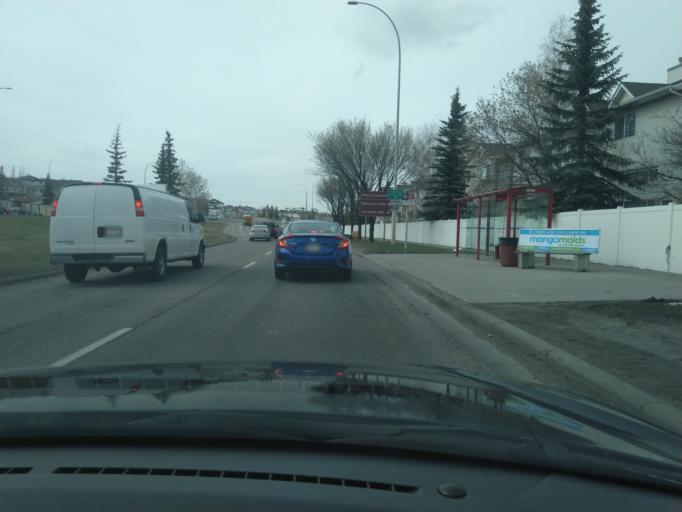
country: CA
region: Alberta
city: Calgary
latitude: 51.1520
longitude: -114.0646
